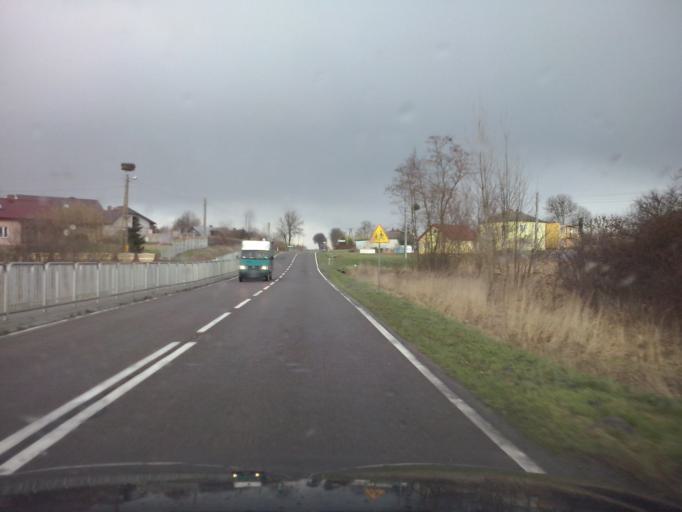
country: PL
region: Lublin Voivodeship
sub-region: Powiat chelmski
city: Rejowiec
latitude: 51.0328
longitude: 23.2412
